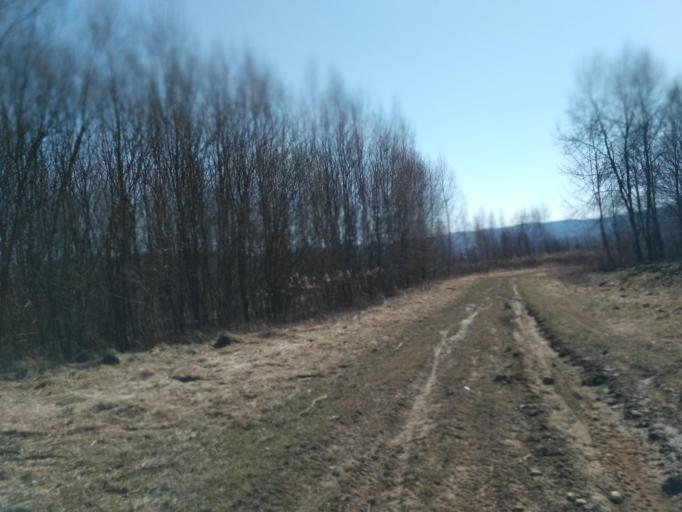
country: PL
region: Subcarpathian Voivodeship
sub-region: Powiat brzozowski
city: Domaradz
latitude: 49.7949
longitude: 21.9772
